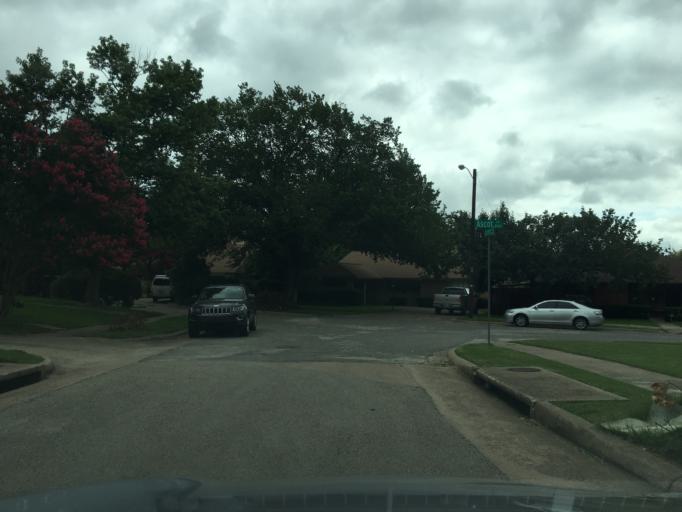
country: US
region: Texas
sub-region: Dallas County
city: Highland Park
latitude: 32.8540
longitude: -96.7450
